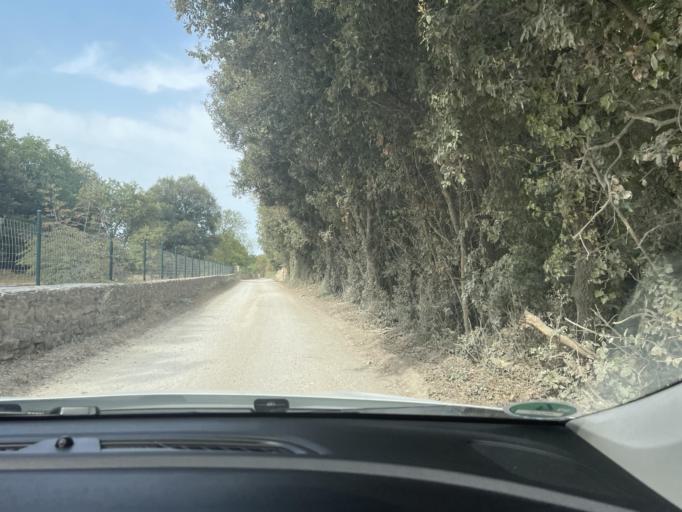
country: HR
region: Istarska
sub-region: Grad Rovinj
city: Rovinj
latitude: 45.0413
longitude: 13.7064
